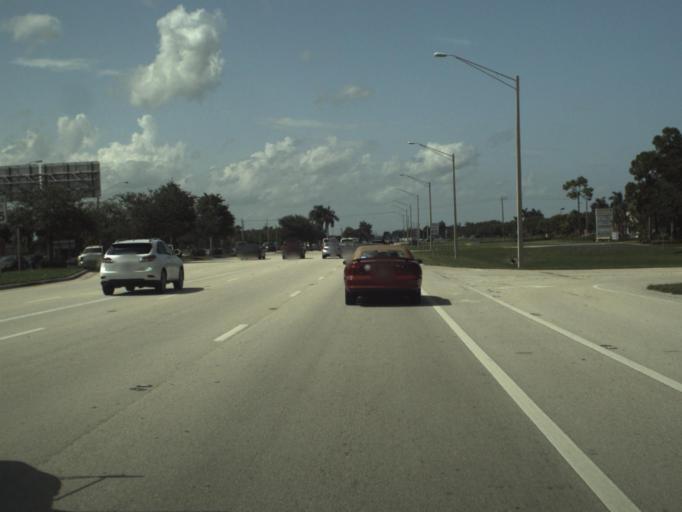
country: US
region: Florida
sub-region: Palm Beach County
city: Royal Palm Beach
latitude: 26.6817
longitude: -80.2021
